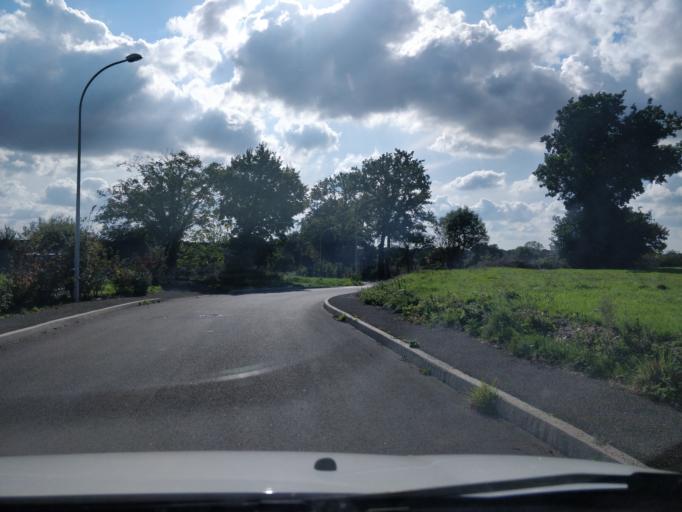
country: FR
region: Brittany
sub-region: Departement d'Ille-et-Vilaine
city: Saint-Aubin-du-Cormier
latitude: 48.2556
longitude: -1.4159
